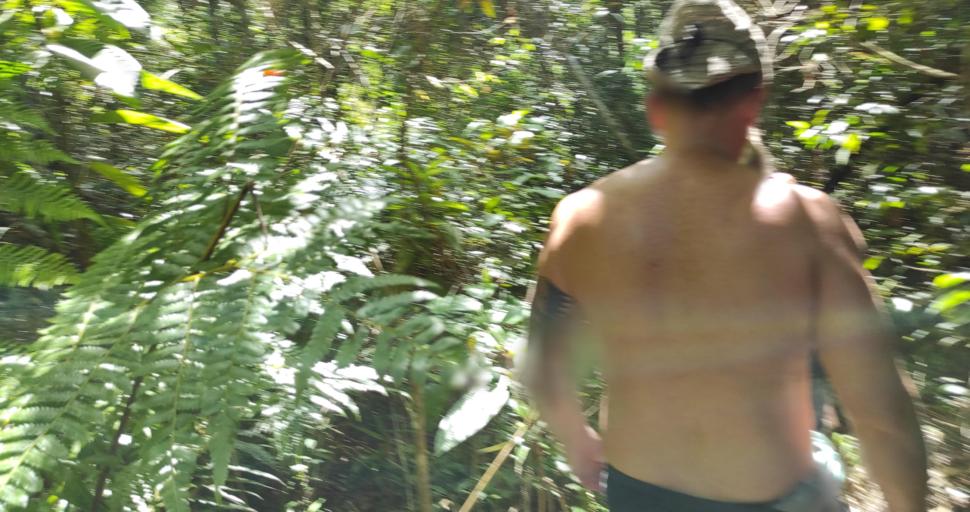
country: BR
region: Santa Catarina
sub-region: Porto Belo
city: Porto Belo
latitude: -27.1951
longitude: -48.5600
